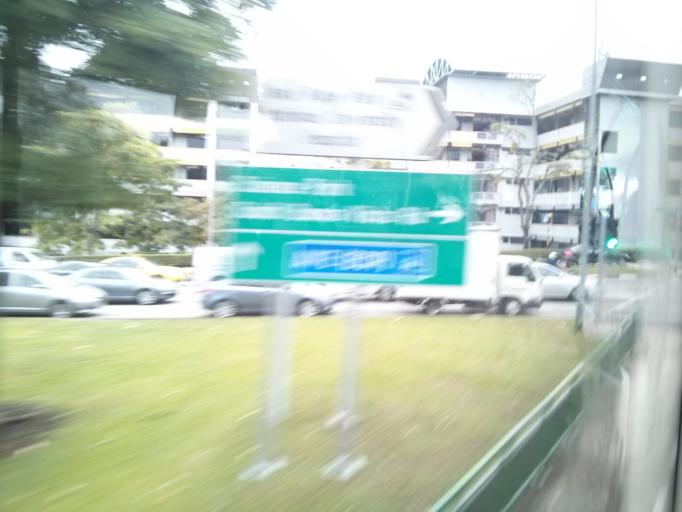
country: SG
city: Singapore
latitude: 1.2955
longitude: 103.7858
